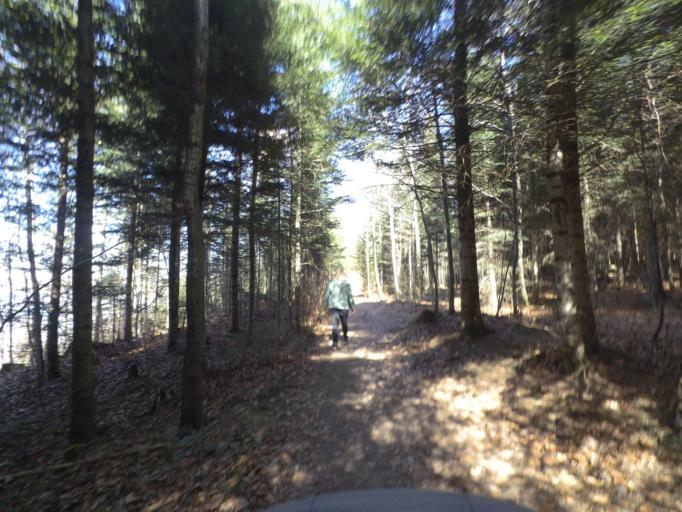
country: AT
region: Salzburg
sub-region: Politischer Bezirk Salzburg-Umgebung
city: Mattsee
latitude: 47.9906
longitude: 13.1008
